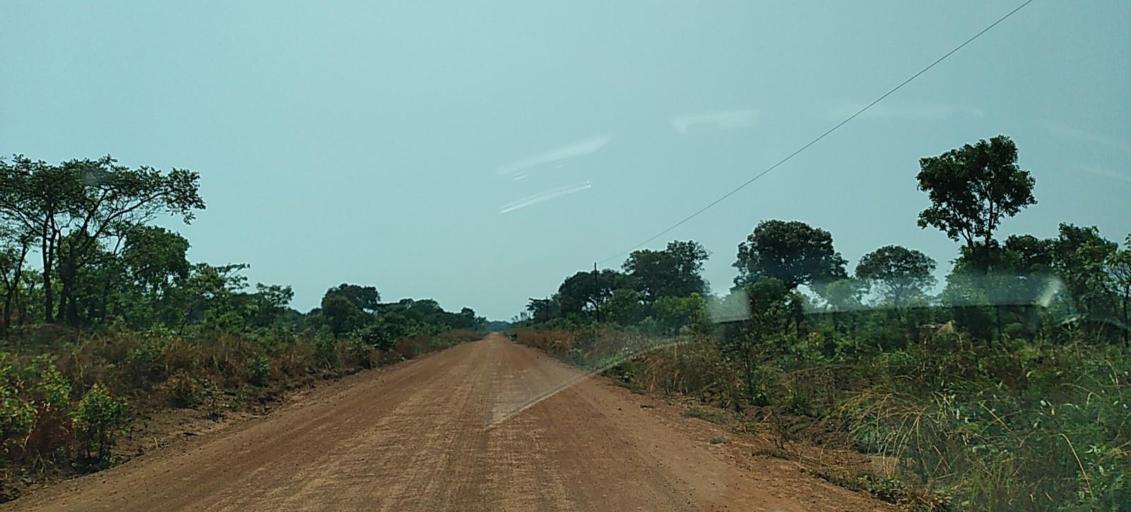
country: ZM
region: North-Western
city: Kansanshi
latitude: -11.9937
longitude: 26.6373
